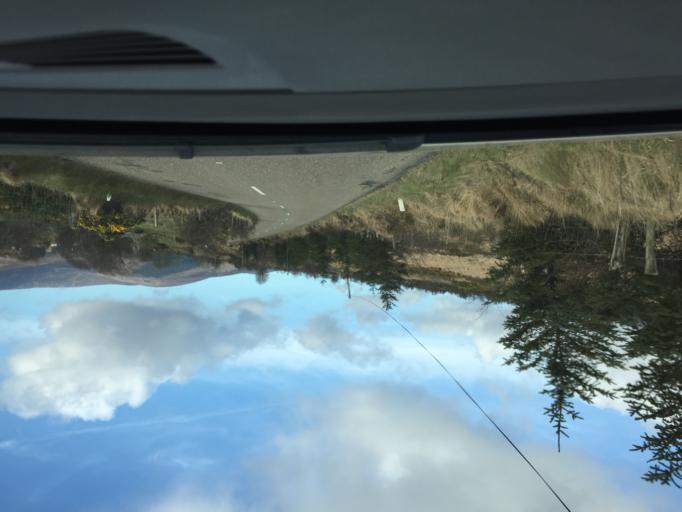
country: IE
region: Leinster
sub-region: Wicklow
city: Valleymount
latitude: 53.0620
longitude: -6.5088
